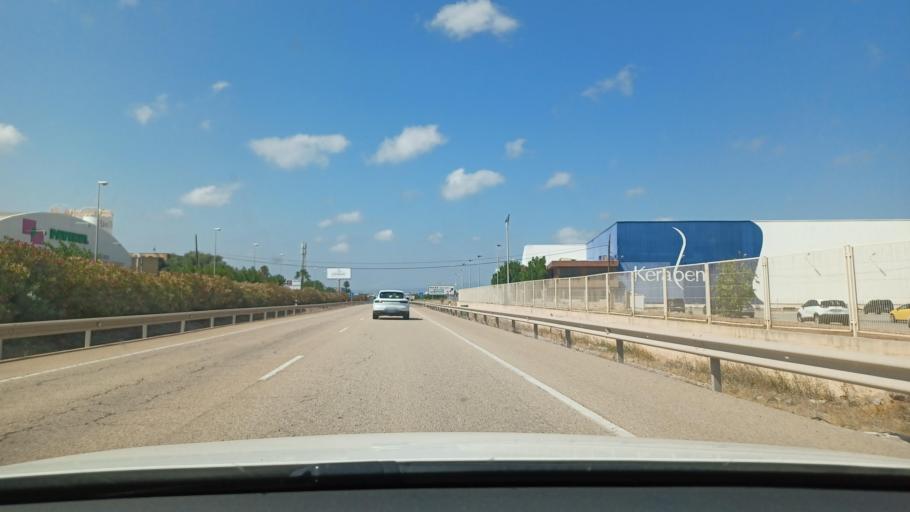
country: ES
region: Valencia
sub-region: Provincia de Castello
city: Moncofar
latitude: 39.8273
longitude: -0.1651
